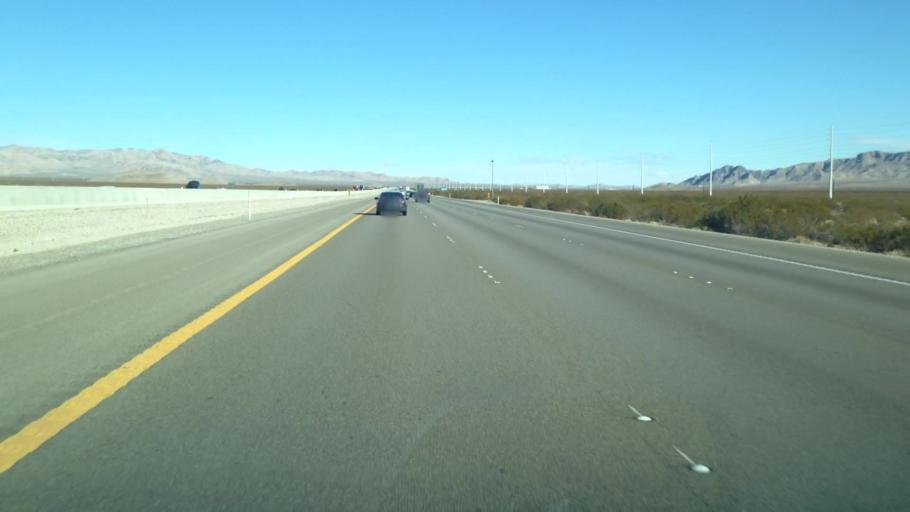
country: US
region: Nevada
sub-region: Clark County
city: Sandy Valley
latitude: 35.7034
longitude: -115.3690
